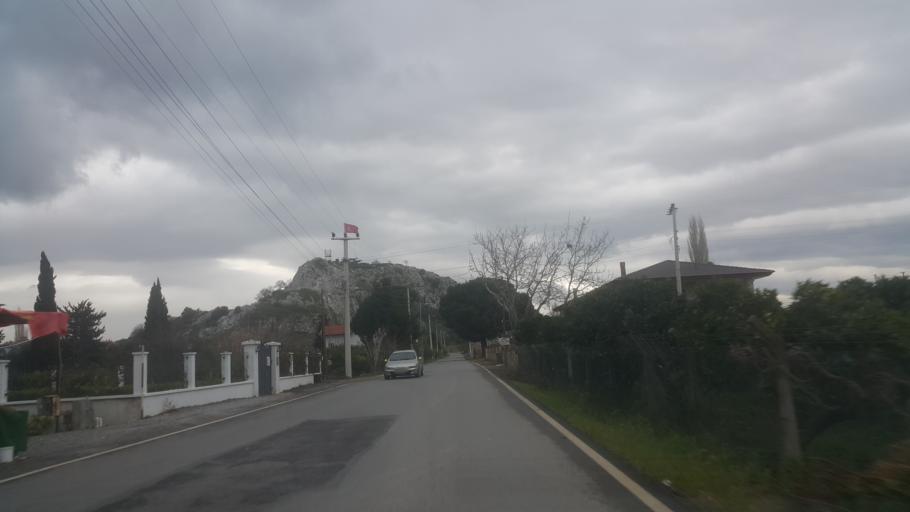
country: TR
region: Izmir
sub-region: Seferihisar
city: Seferhisar
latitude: 38.1907
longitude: 26.8023
